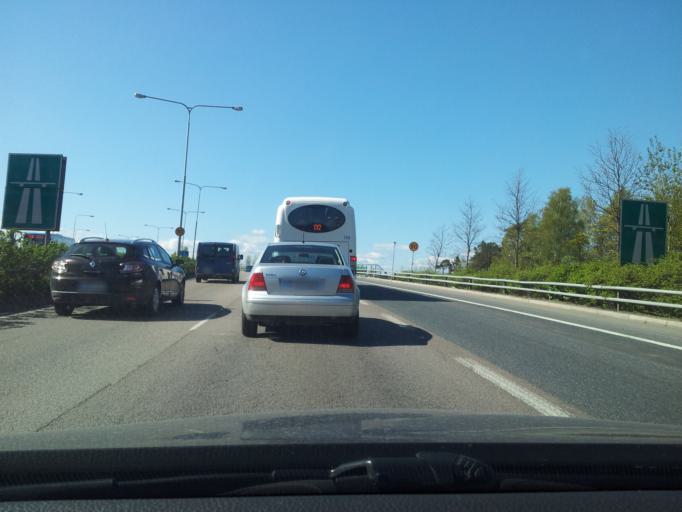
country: FI
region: Uusimaa
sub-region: Helsinki
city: Helsinki
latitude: 60.1651
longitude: 24.9119
